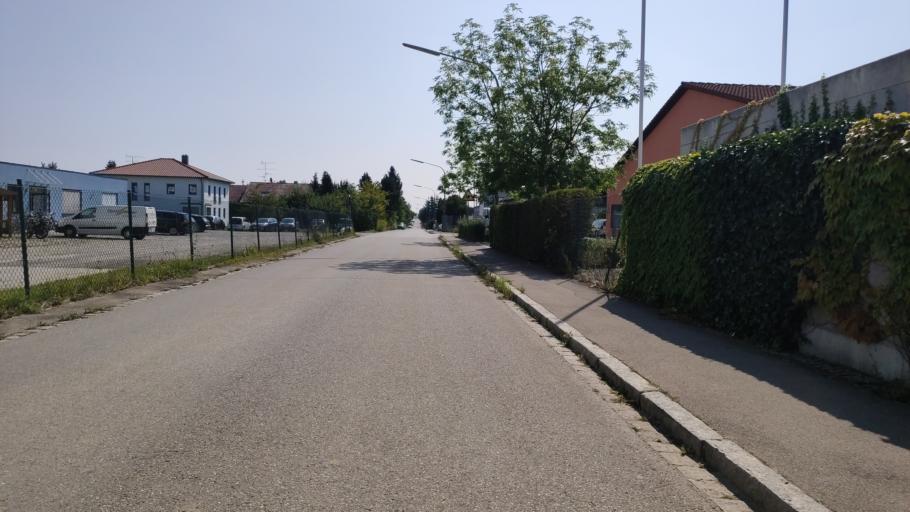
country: DE
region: Bavaria
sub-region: Swabia
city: Bobingen
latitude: 48.2695
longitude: 10.8418
